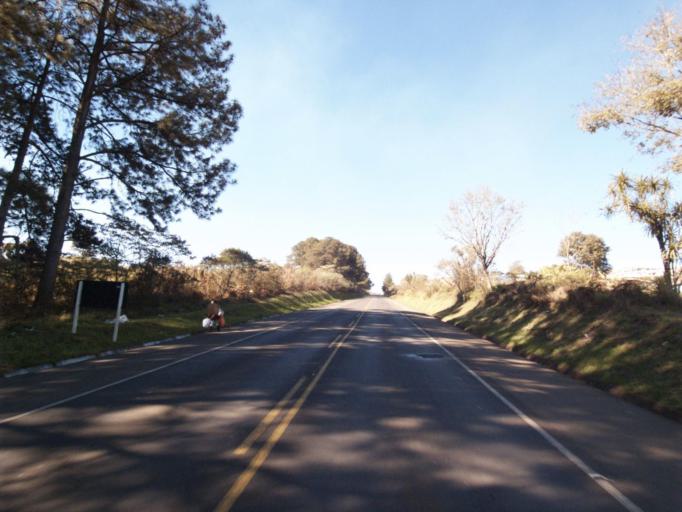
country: BR
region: Santa Catarina
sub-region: Chapeco
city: Chapeco
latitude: -27.0005
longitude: -52.6569
